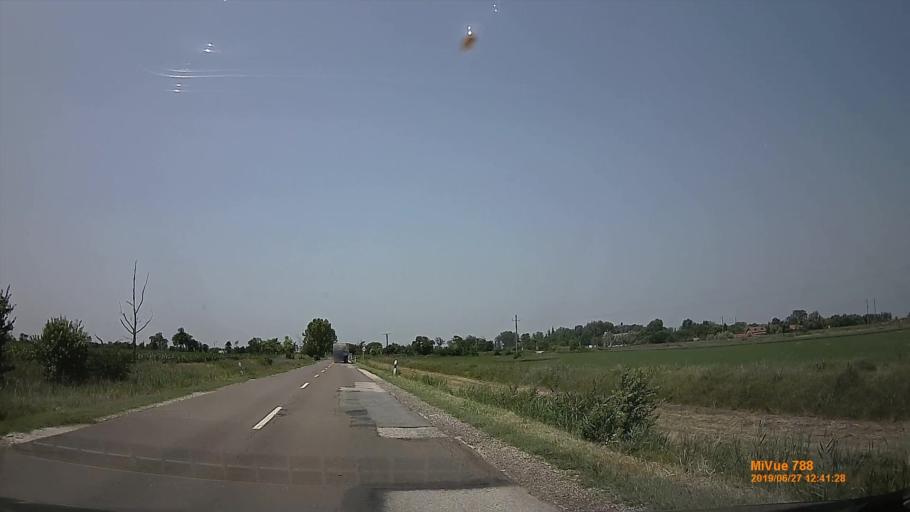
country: HU
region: Pest
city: Tortel
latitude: 47.1807
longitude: 19.8967
